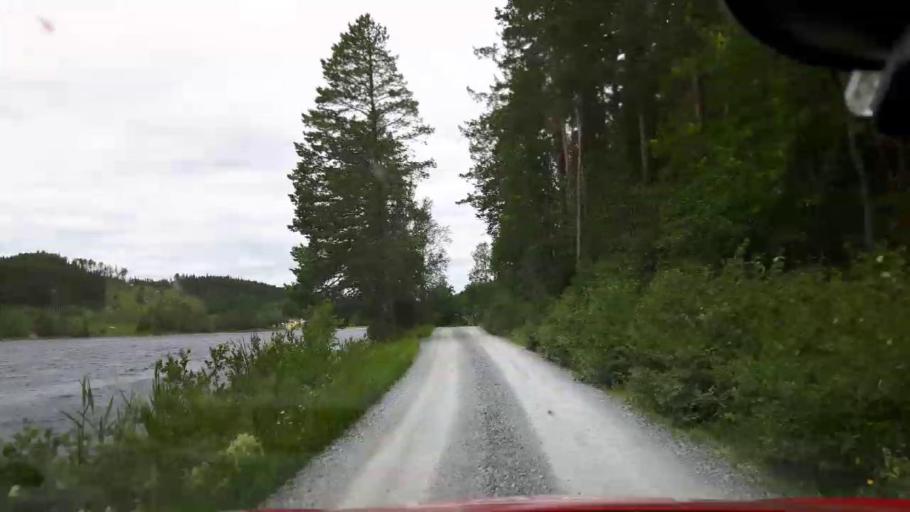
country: SE
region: Jaemtland
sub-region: OEstersunds Kommun
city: Brunflo
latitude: 63.0270
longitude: 14.9379
